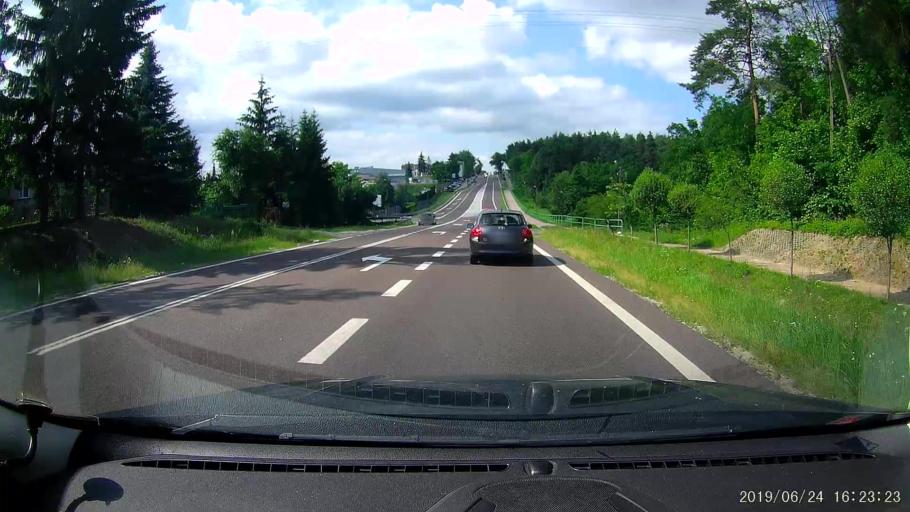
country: PL
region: Lublin Voivodeship
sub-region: Powiat tomaszowski
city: Tomaszow Lubelski
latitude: 50.4309
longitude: 23.4218
